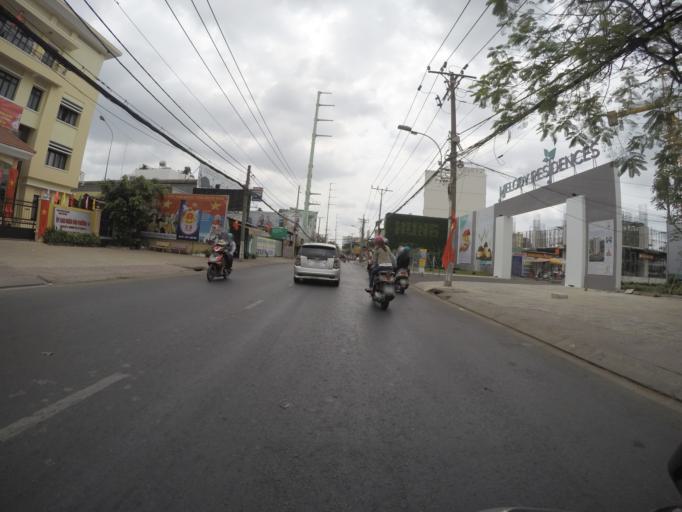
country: VN
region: Ho Chi Minh City
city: Quan Tan Phu
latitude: 10.7964
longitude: 106.6380
